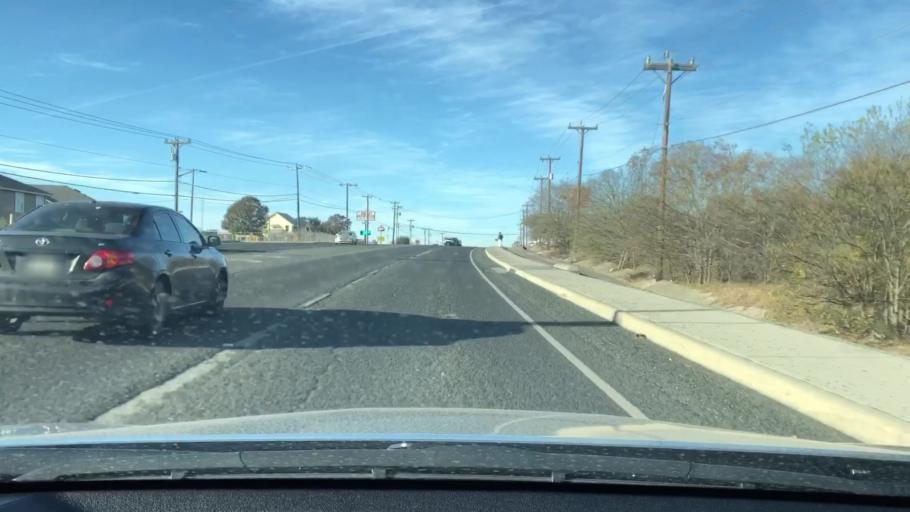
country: US
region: Texas
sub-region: Bexar County
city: Converse
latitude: 29.5010
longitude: -98.3155
